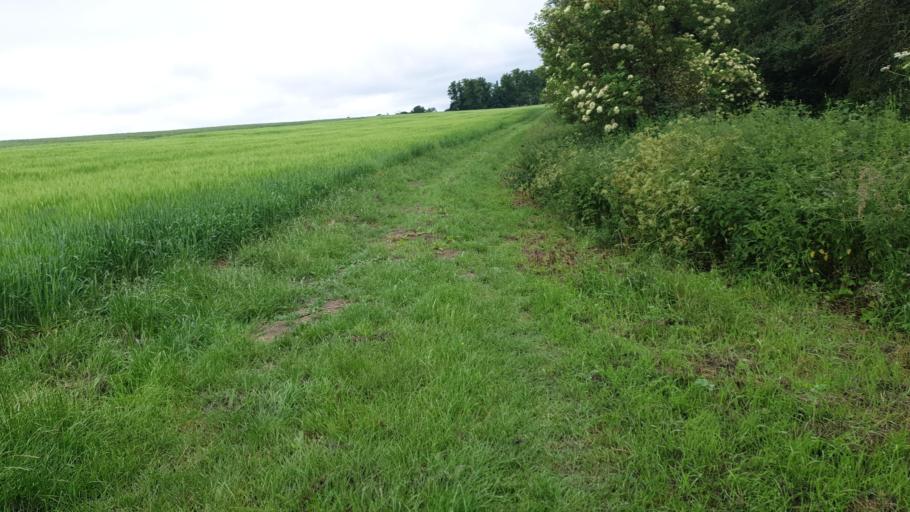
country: GB
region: England
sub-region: Essex
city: Great Bentley
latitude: 51.8843
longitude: 1.0887
